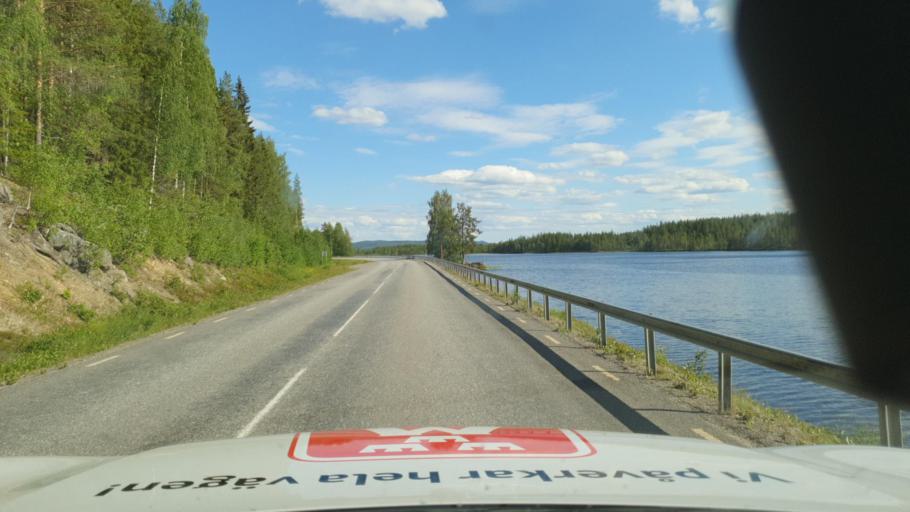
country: SE
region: Vaesterbotten
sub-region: Norsjo Kommun
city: Norsjoe
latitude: 64.8600
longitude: 19.7298
